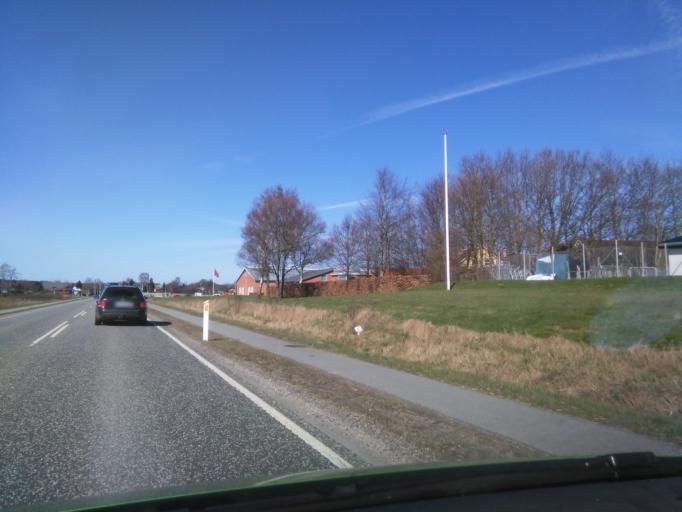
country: DK
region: Central Jutland
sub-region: Favrskov Kommune
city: Hinnerup
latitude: 56.2511
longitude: 10.0696
